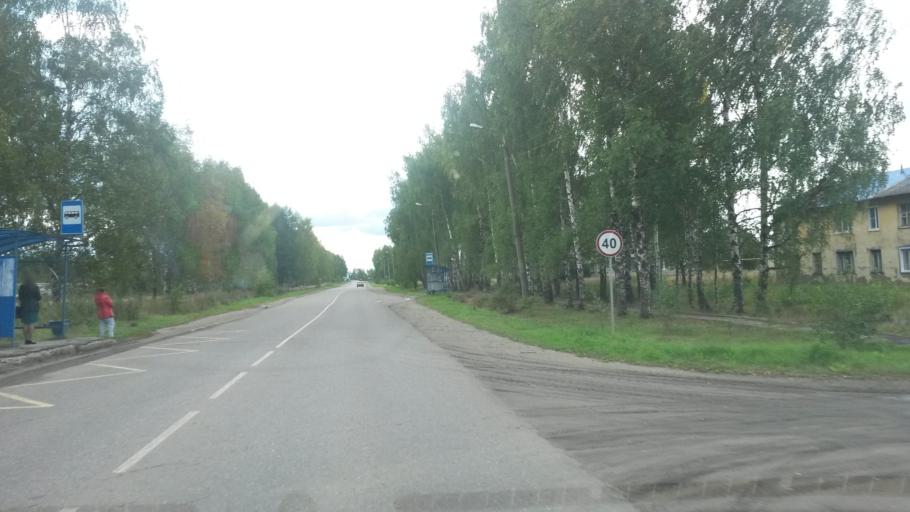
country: RU
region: Ivanovo
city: Zavolzhsk
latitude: 57.4719
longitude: 42.1579
